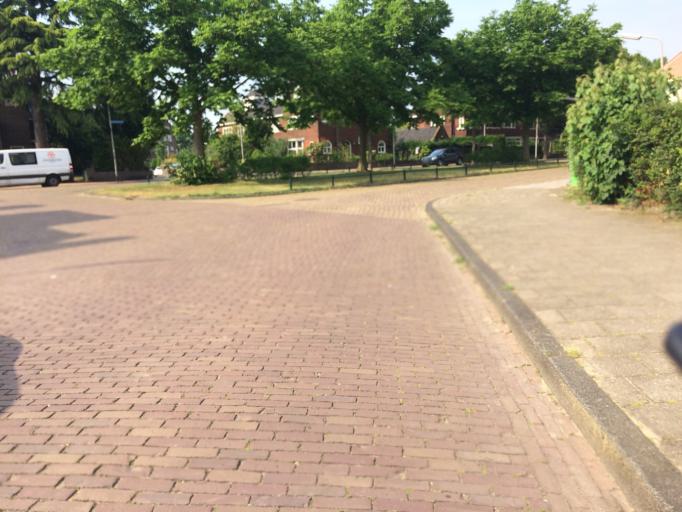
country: NL
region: Gelderland
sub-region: Gemeente Nijmegen
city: Nijmegen
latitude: 51.8351
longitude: 5.8637
